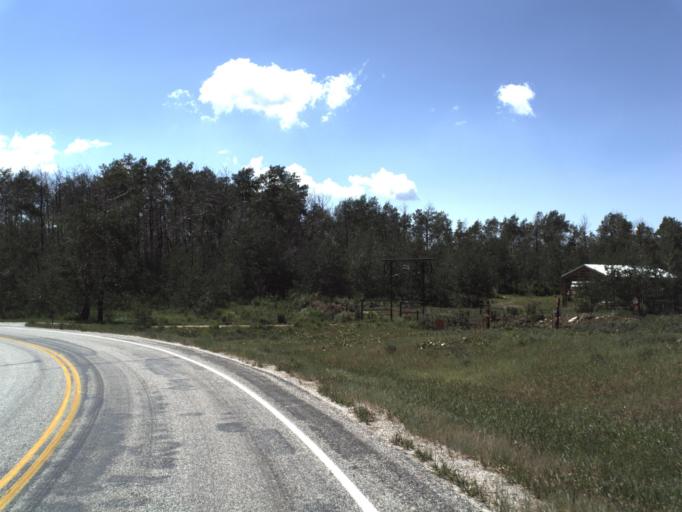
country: US
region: Utah
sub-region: Weber County
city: Wolf Creek
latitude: 41.4207
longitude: -111.5633
